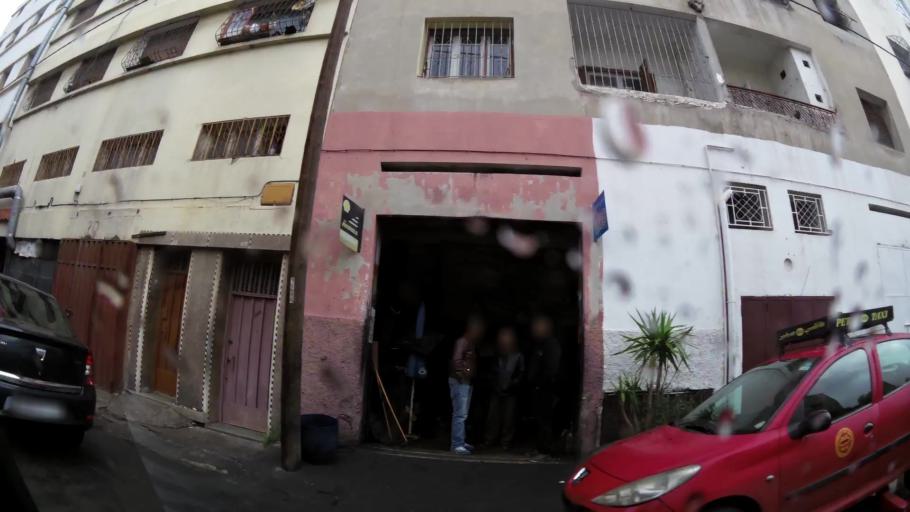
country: MA
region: Grand Casablanca
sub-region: Casablanca
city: Casablanca
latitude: 33.5701
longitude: -7.5931
